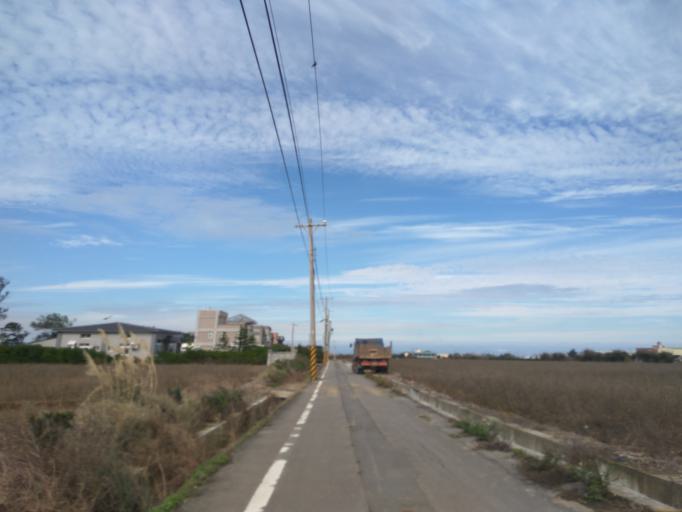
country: TW
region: Taiwan
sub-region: Hsinchu
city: Zhubei
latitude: 25.0078
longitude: 121.0744
